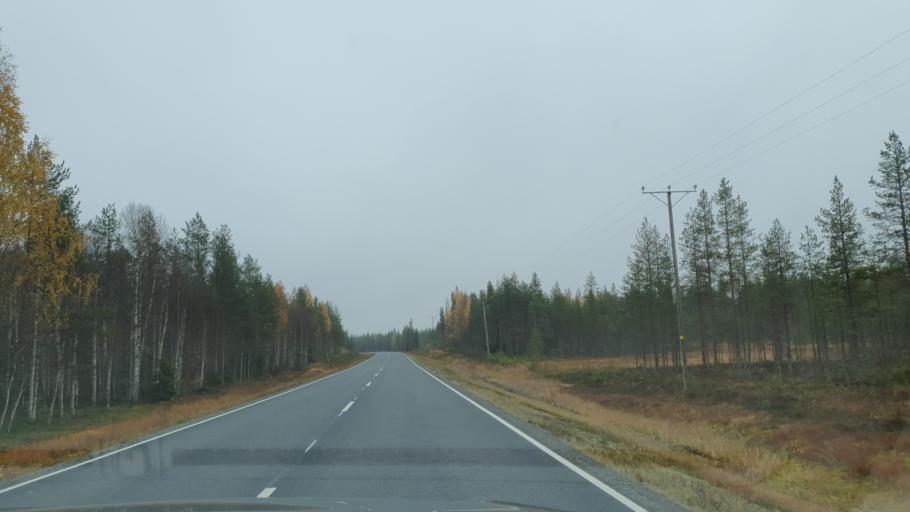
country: FI
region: Lapland
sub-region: Rovaniemi
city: Ranua
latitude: 66.1371
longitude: 26.2748
